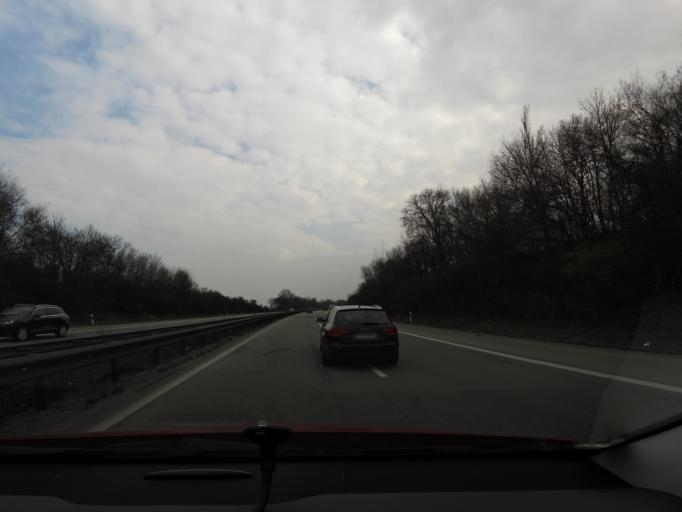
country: DE
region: Rheinland-Pfalz
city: Wallertheim
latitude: 49.8267
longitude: 8.0430
